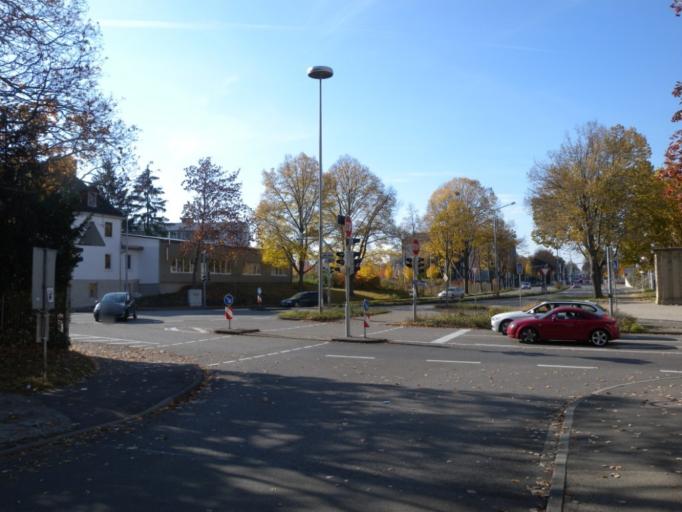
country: DE
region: Baden-Wuerttemberg
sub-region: Regierungsbezirk Stuttgart
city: Ludwigsburg
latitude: 48.8906
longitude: 9.1840
